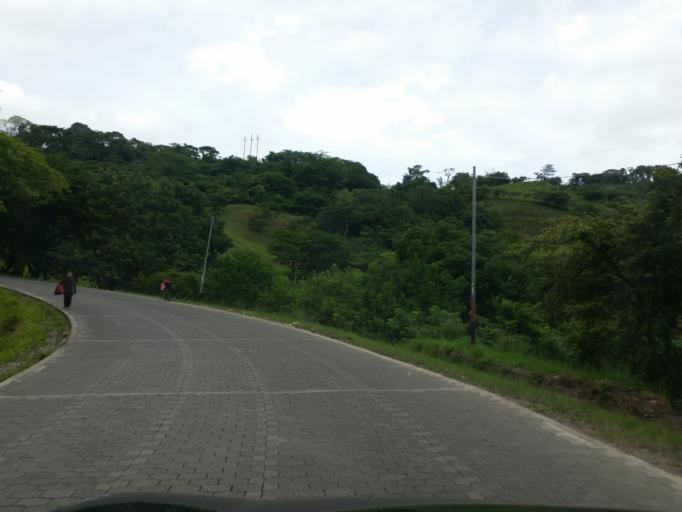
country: NI
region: Matagalpa
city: San Ramon
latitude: 12.9304
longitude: -85.8476
